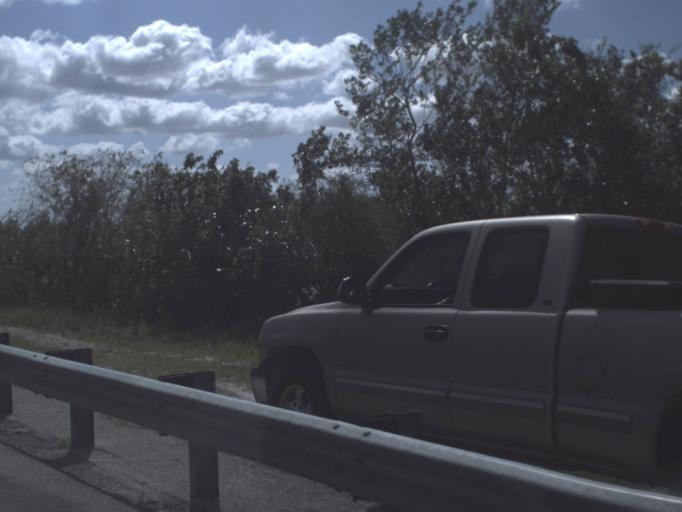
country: US
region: Florida
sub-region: Collier County
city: Marco
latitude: 25.9650
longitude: -81.5274
